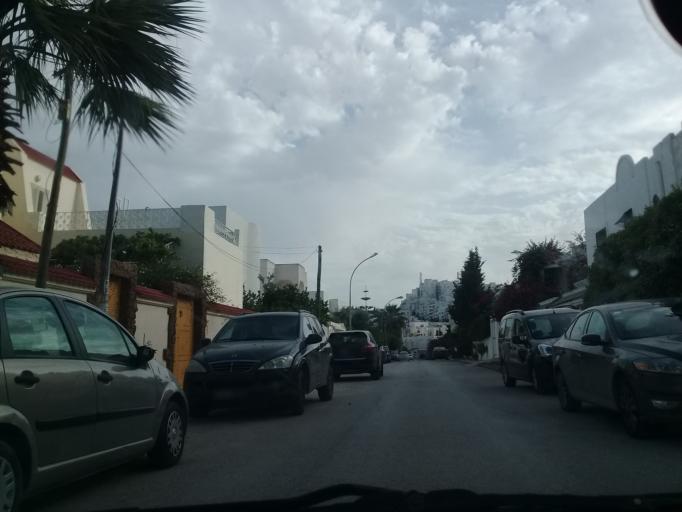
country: TN
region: Ariana
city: Ariana
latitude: 36.8620
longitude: 10.1671
